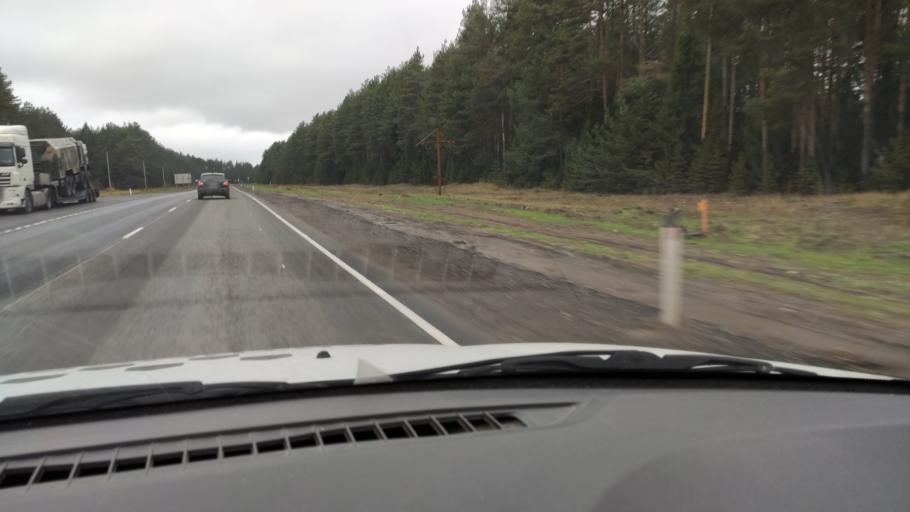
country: RU
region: Kirov
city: Belaya Kholunitsa
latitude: 58.8443
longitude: 50.8101
